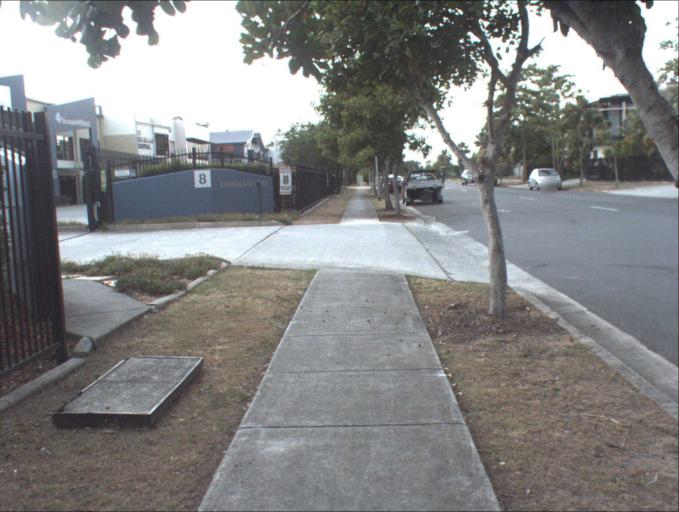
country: AU
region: Queensland
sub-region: Logan
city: Beenleigh
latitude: -27.6837
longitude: 153.1912
